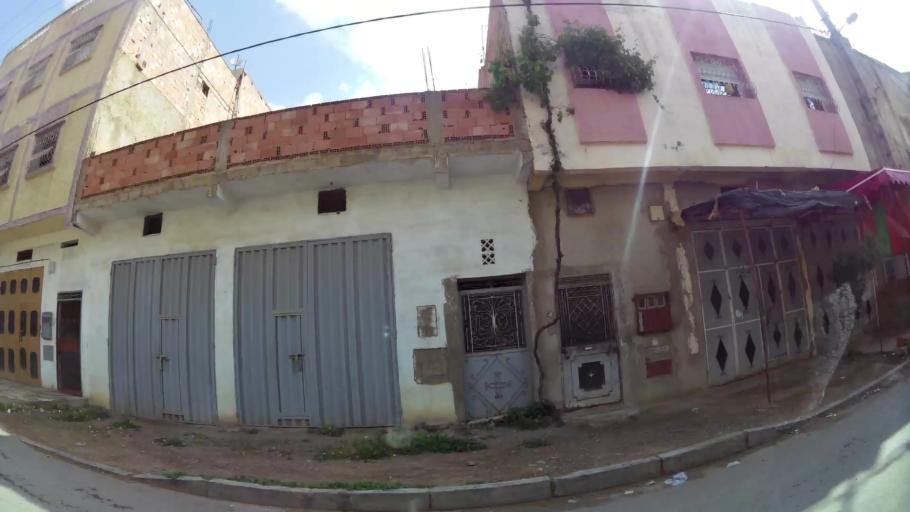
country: MA
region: Rabat-Sale-Zemmour-Zaer
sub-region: Khemisset
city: Tiflet
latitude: 33.8957
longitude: -6.3190
